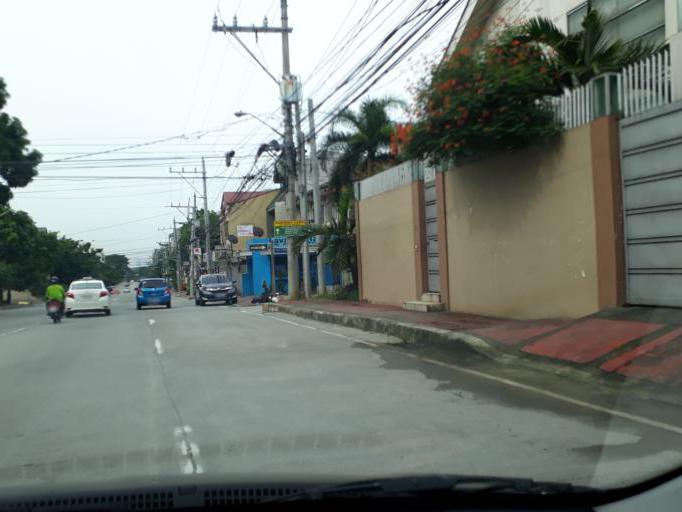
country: PH
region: Calabarzon
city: Del Monte
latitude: 14.6339
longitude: 121.0307
